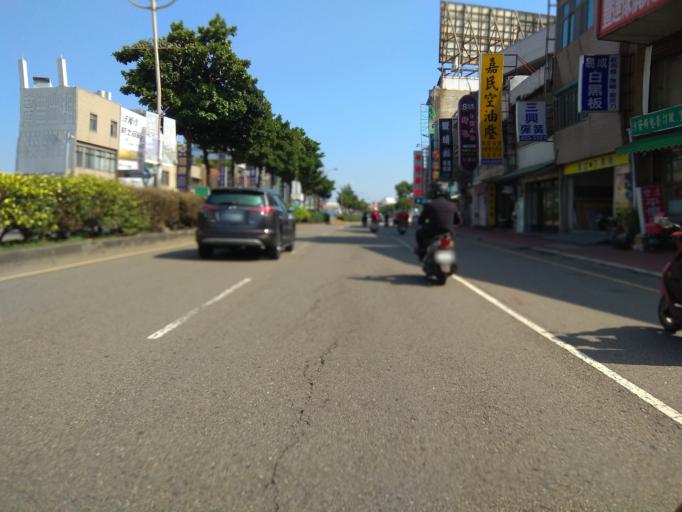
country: TW
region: Taiwan
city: Taoyuan City
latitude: 24.9634
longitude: 121.2317
